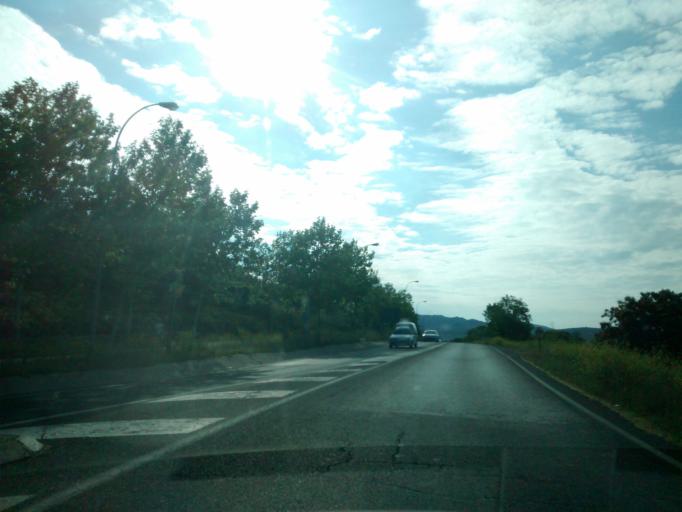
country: ES
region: Madrid
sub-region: Provincia de Madrid
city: Alpedrete
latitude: 40.6532
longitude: -4.0197
